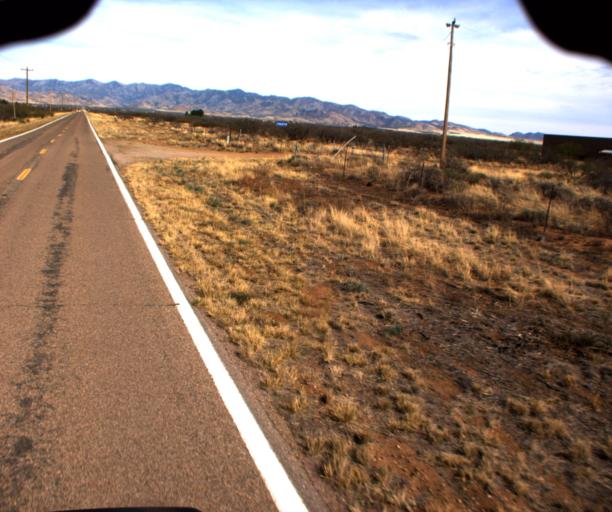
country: US
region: Arizona
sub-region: Cochise County
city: Willcox
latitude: 31.8760
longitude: -109.5599
